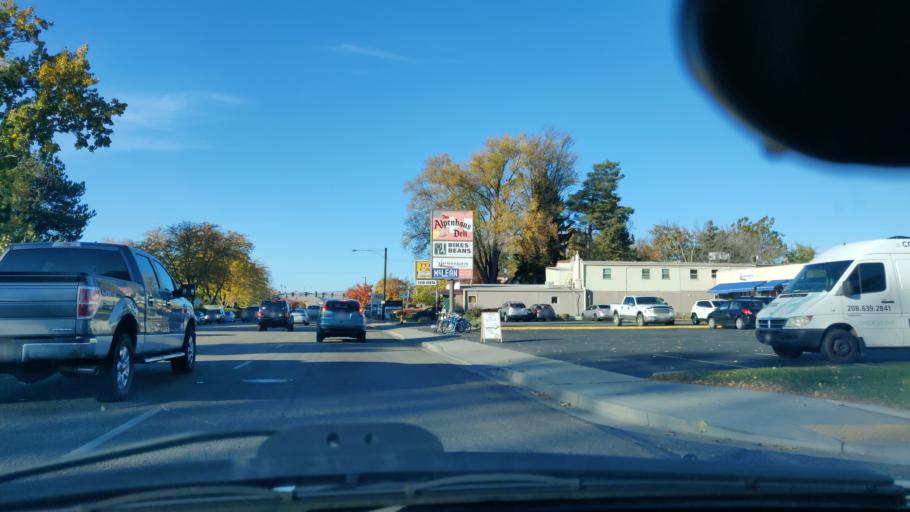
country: US
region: Idaho
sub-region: Ada County
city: Boise
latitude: 43.5916
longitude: -116.2136
